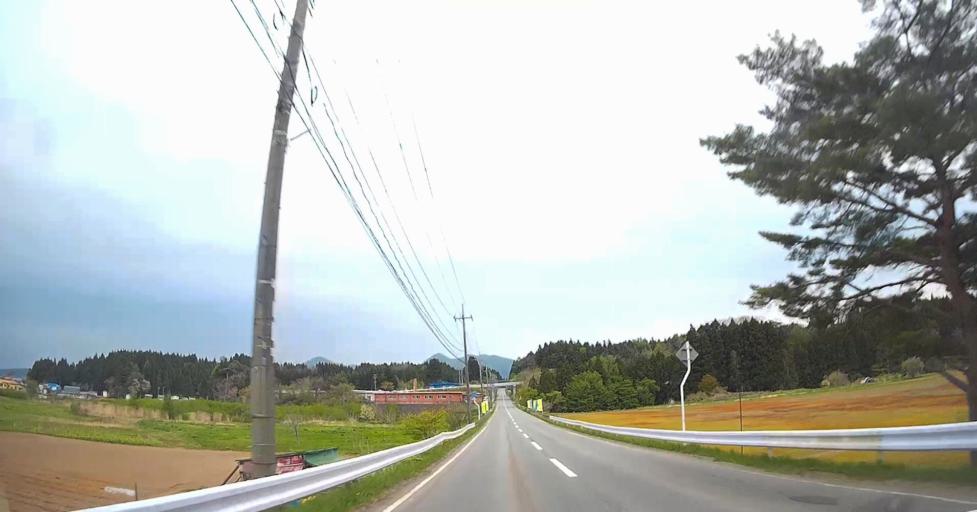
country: JP
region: Aomori
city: Goshogawara
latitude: 41.1780
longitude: 140.4764
